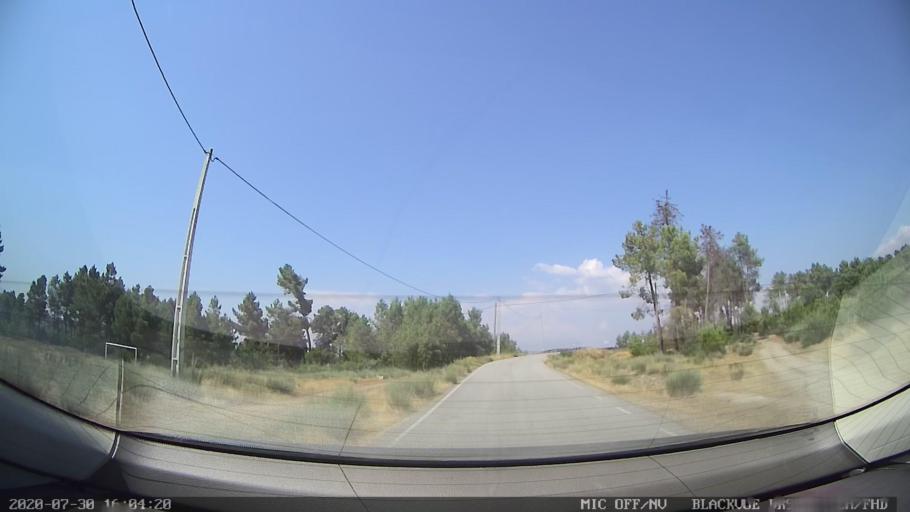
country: PT
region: Vila Real
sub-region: Murca
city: Murca
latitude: 41.3522
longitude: -7.4861
